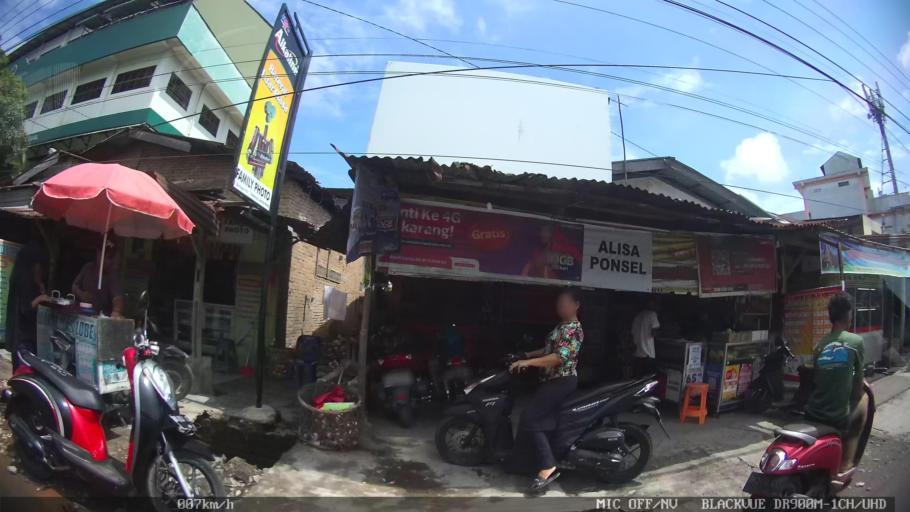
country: ID
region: North Sumatra
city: Medan
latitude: 3.5909
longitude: 98.7554
